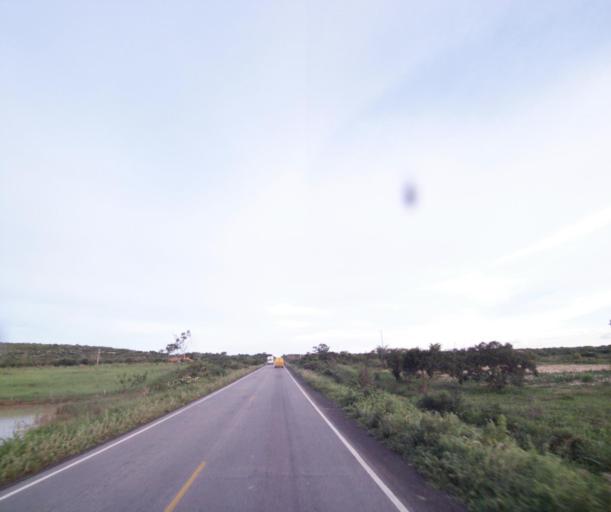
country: BR
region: Bahia
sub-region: Brumado
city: Brumado
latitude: -14.2400
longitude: -41.8813
